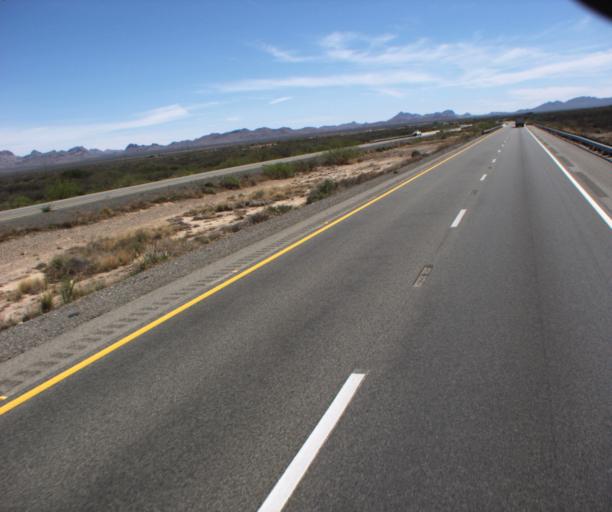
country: US
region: New Mexico
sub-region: Hidalgo County
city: Lordsburg
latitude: 32.2588
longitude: -109.2090
